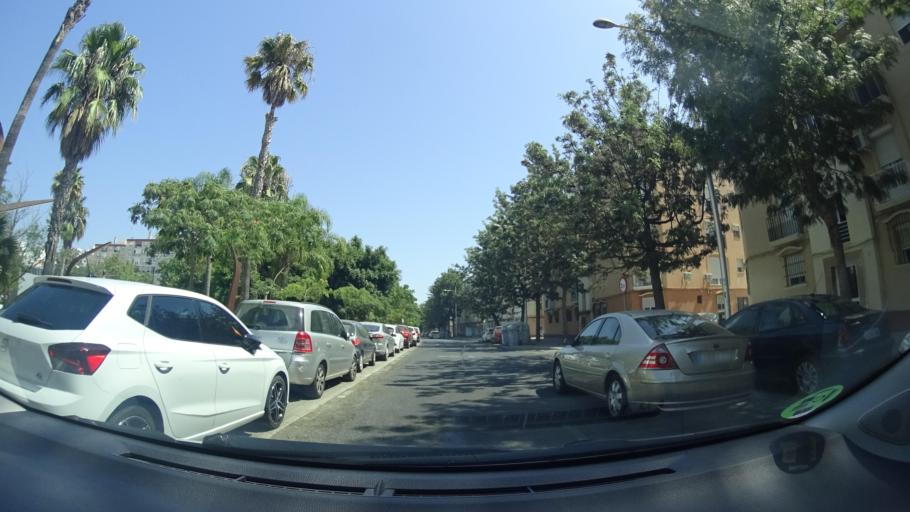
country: ES
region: Andalusia
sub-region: Provincia de Cadiz
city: Cadiz
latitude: 36.5182
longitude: -6.2795
